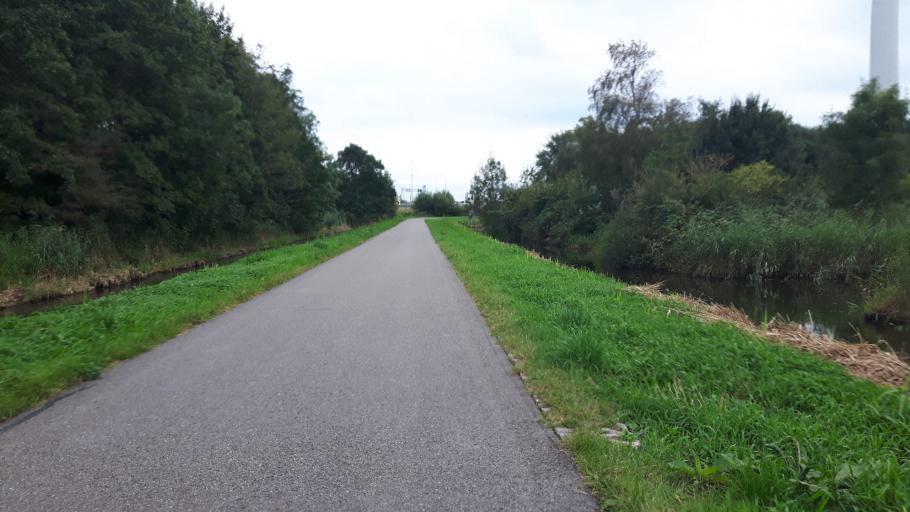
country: NL
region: North Holland
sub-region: Gemeente Ouder-Amstel
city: Ouderkerk aan de Amstel
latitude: 52.2894
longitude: 4.9420
